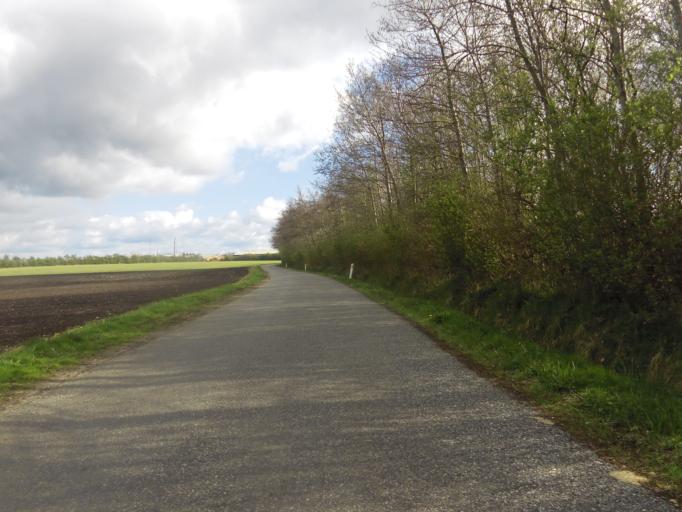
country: DK
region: South Denmark
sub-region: Haderslev Kommune
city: Gram
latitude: 55.2578
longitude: 8.9575
